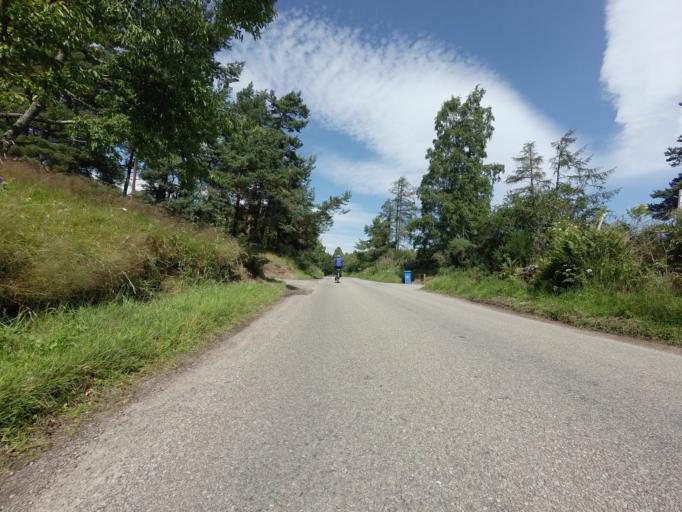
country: GB
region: Scotland
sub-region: Highland
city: Inverness
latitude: 57.5323
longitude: -4.3215
